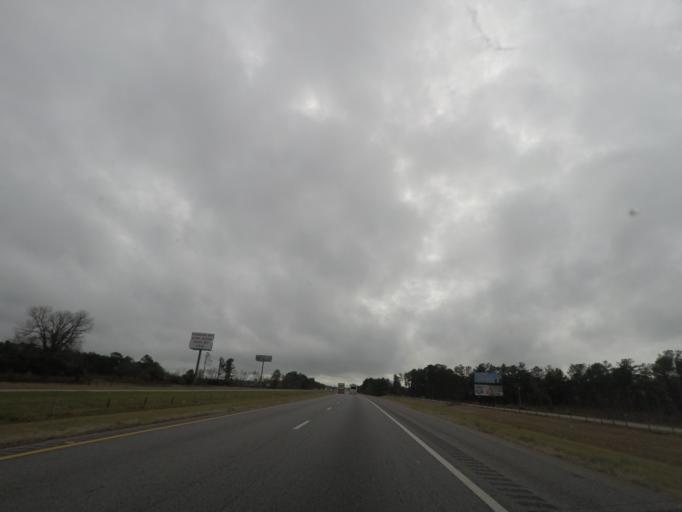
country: US
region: South Carolina
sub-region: Orangeburg County
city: Holly Hill
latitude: 33.3961
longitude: -80.5137
